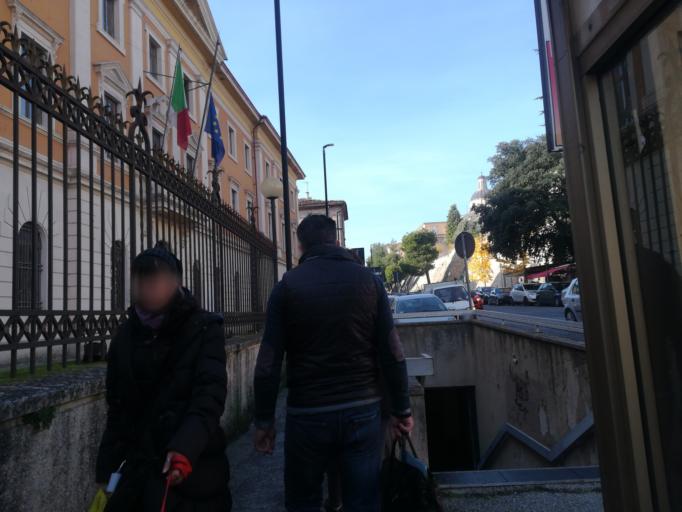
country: IT
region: The Marches
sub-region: Provincia di Macerata
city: Macerata
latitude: 43.2986
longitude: 13.4545
